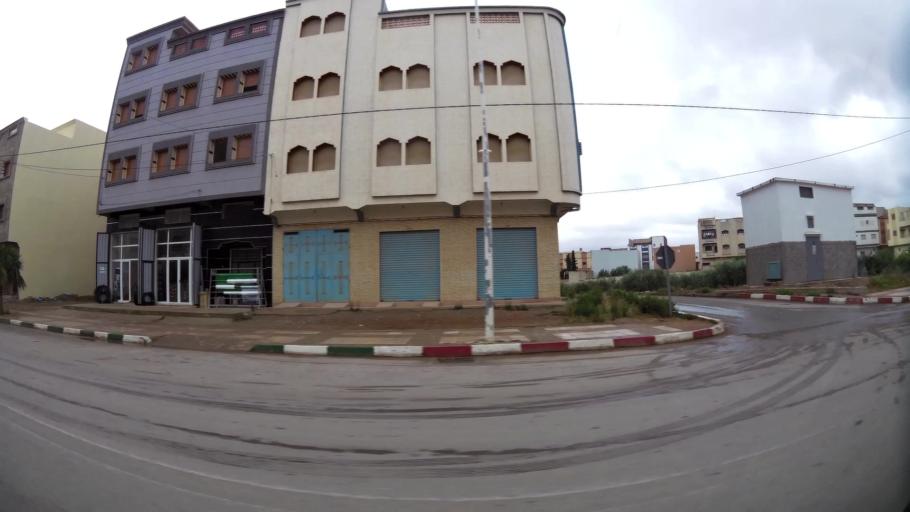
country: MA
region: Oriental
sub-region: Nador
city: Midar
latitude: 35.0488
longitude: -3.4580
